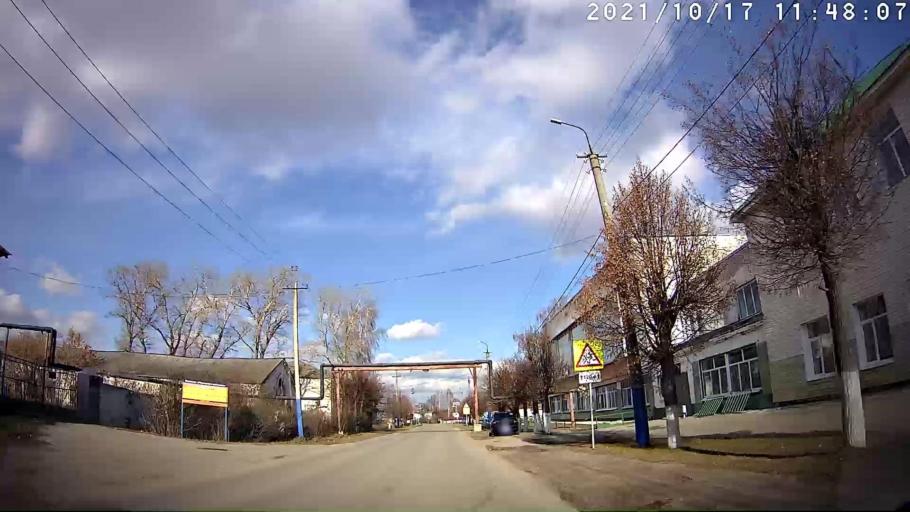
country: RU
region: Mariy-El
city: Kuzhener
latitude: 57.0021
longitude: 48.7338
